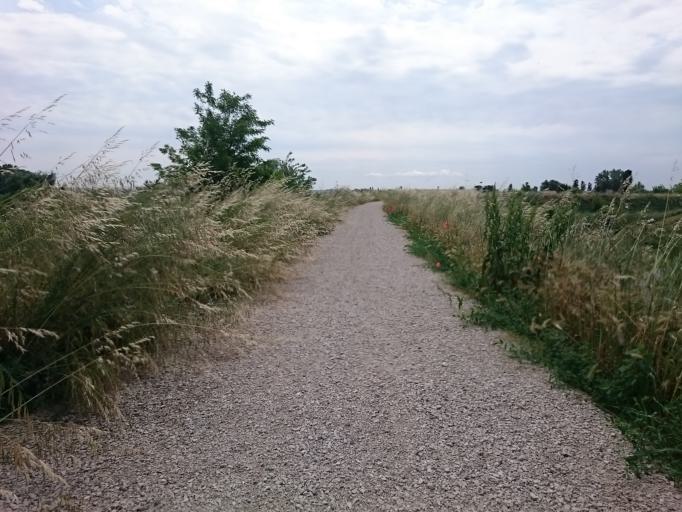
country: IT
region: Veneto
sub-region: Provincia di Padova
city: Carceri
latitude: 45.1940
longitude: 11.6475
